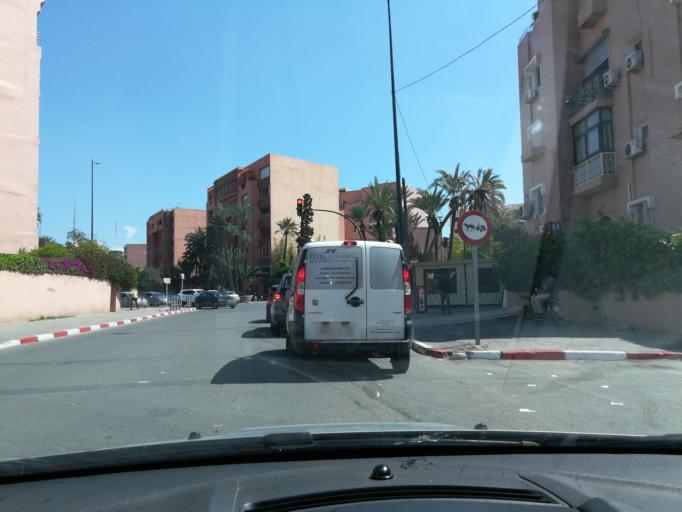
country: MA
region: Marrakech-Tensift-Al Haouz
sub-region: Marrakech
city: Marrakesh
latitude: 31.6383
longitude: -8.0090
